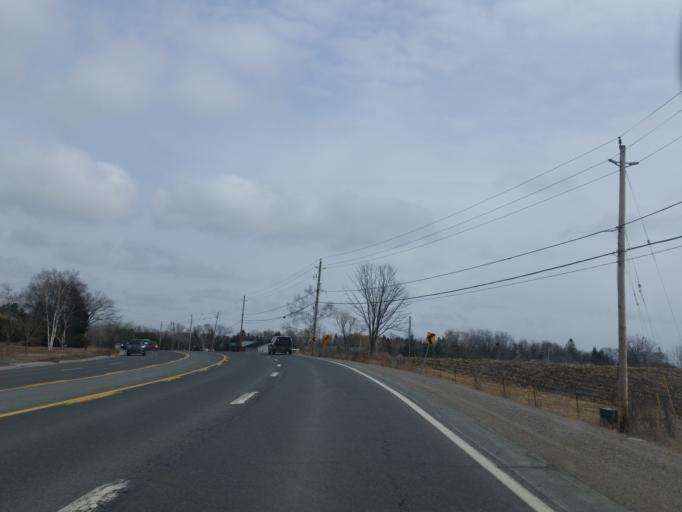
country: CA
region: Ontario
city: Oshawa
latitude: 43.9133
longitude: -78.7602
